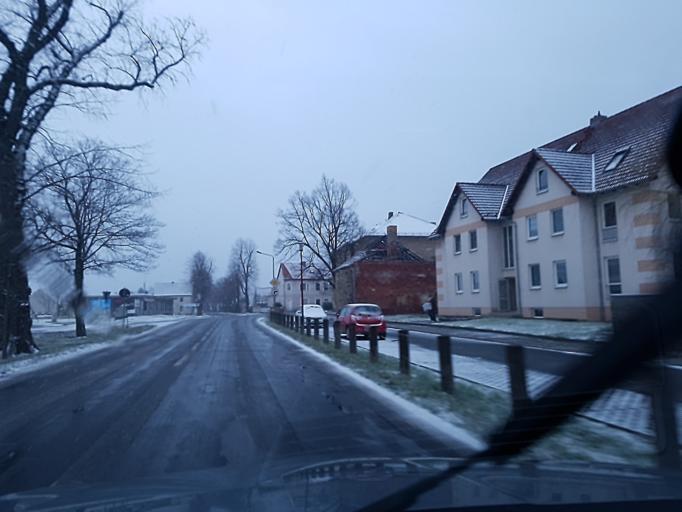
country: DE
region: Brandenburg
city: Elsterwerda
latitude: 51.4513
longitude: 13.5282
